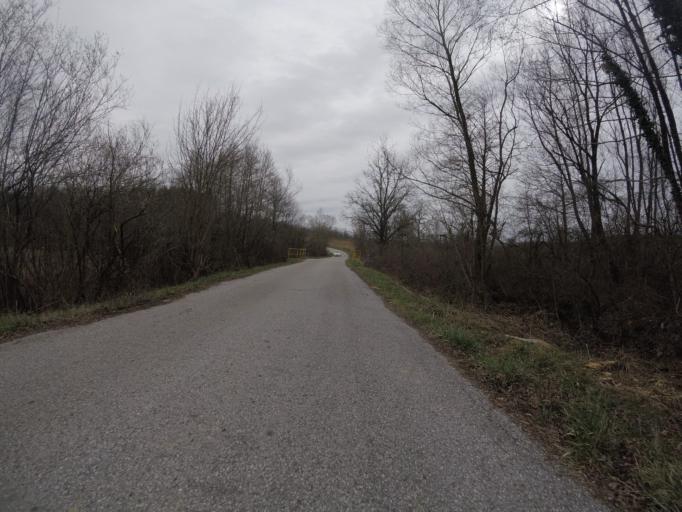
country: HR
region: Zagrebacka
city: Lukavec
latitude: 45.5661
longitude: 15.9658
